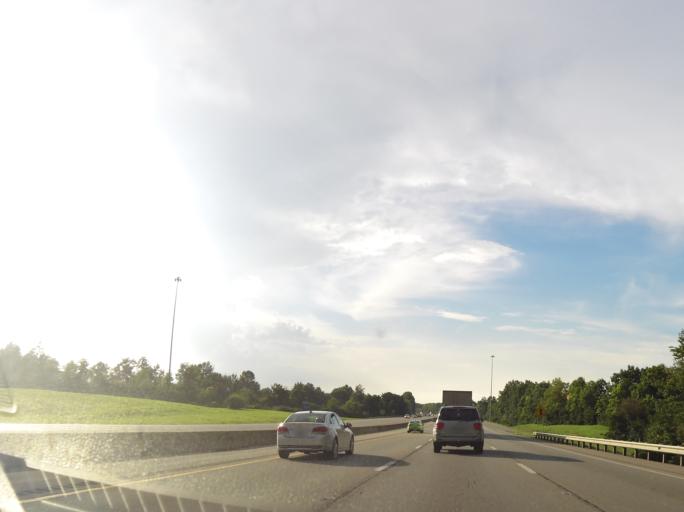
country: US
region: Kentucky
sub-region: Fayette County
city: Lexington-Fayette
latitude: 38.0791
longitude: -84.4583
